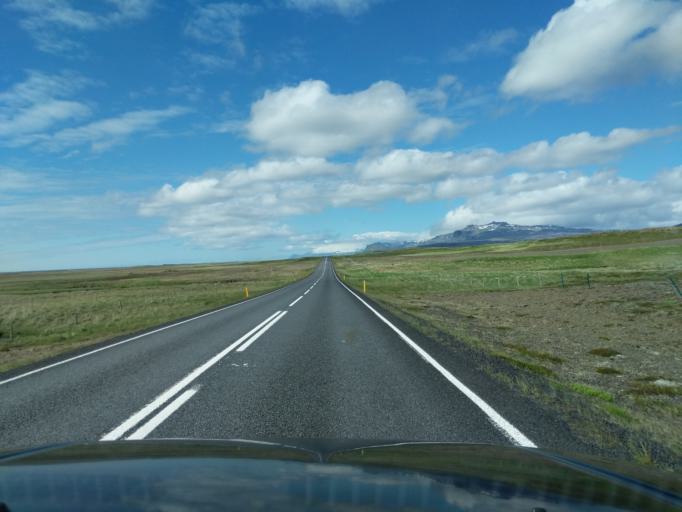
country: IS
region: West
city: Stykkisholmur
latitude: 64.8423
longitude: -22.5992
